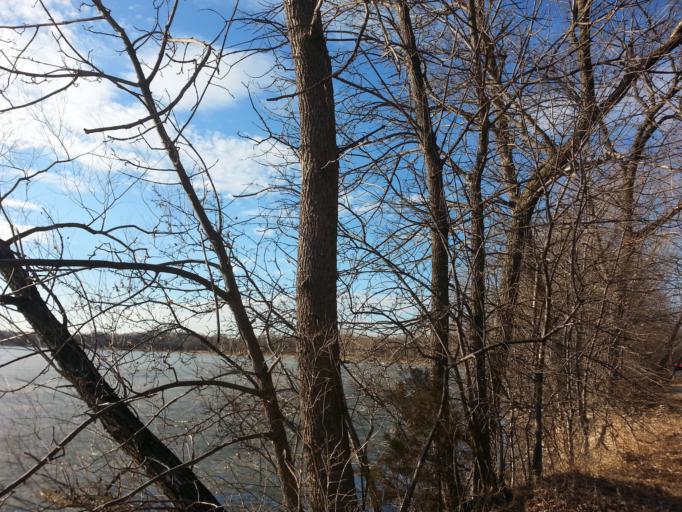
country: US
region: Minnesota
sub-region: Hennepin County
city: Richfield
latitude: 44.9238
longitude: -93.2969
